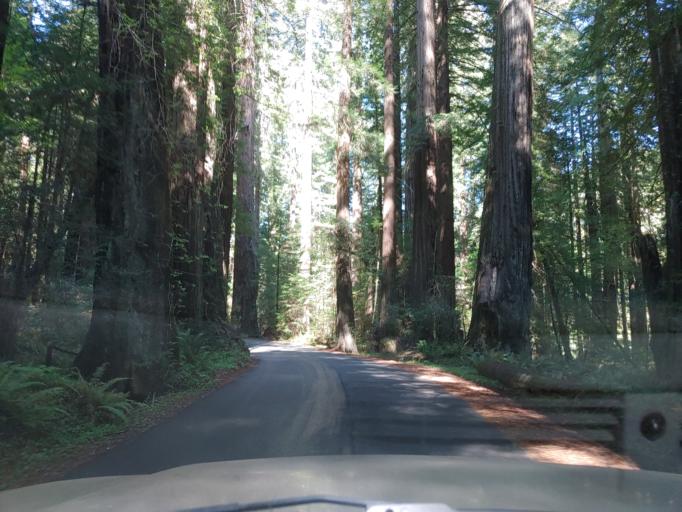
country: US
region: California
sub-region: Humboldt County
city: Rio Dell
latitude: 40.3458
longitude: -123.9339
